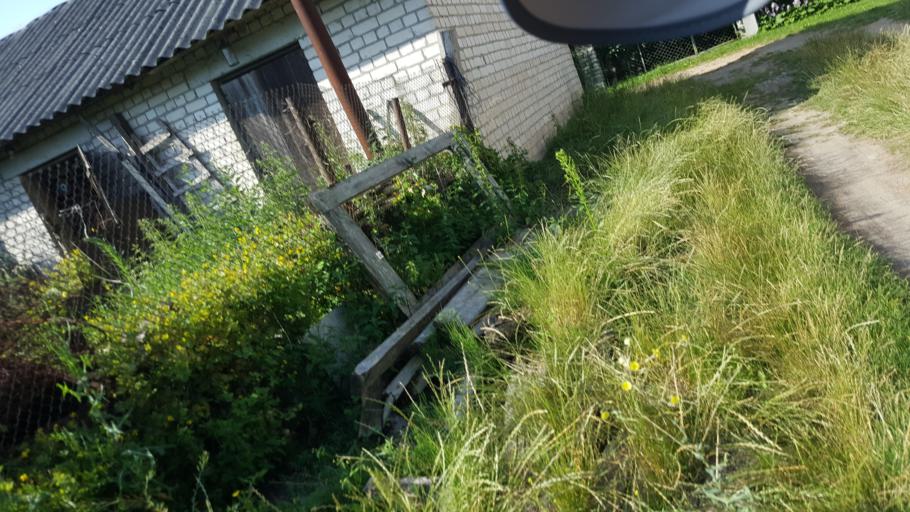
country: BY
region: Brest
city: Kamyanyets
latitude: 52.3929
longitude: 23.8331
